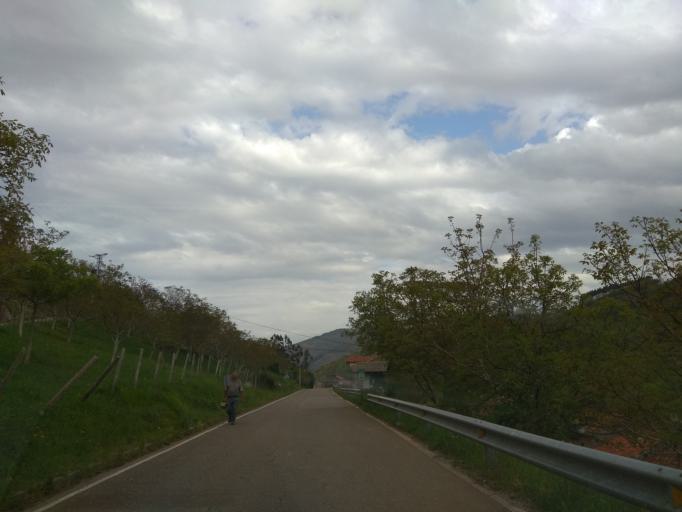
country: ES
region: Cantabria
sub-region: Provincia de Cantabria
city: Cabezon de Liebana
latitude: 43.2547
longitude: -4.5126
